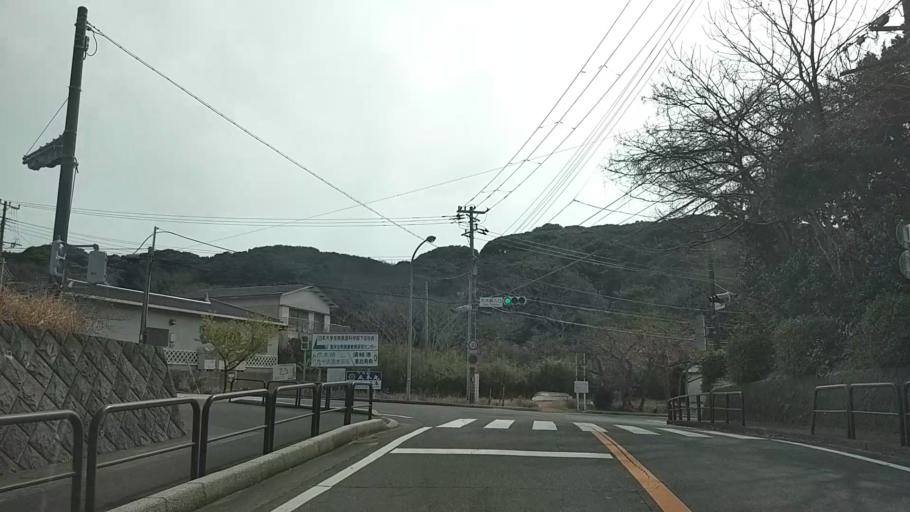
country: JP
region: Shizuoka
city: Shimoda
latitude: 34.6640
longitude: 138.9644
